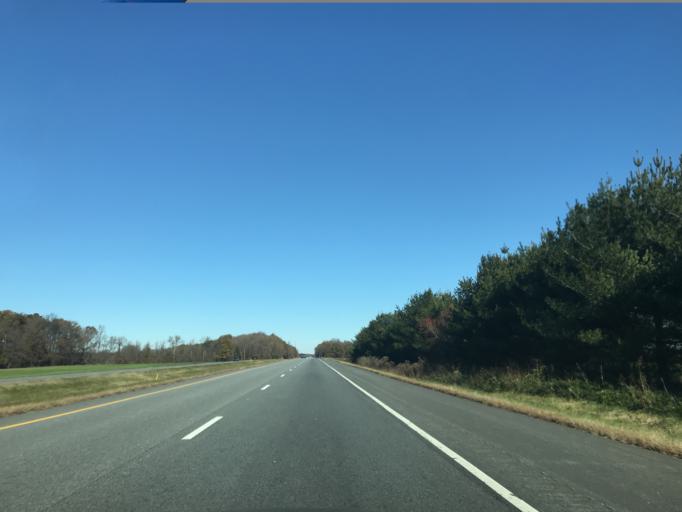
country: US
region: Maryland
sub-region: Queen Anne's County
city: Kingstown
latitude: 39.1471
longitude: -75.9228
